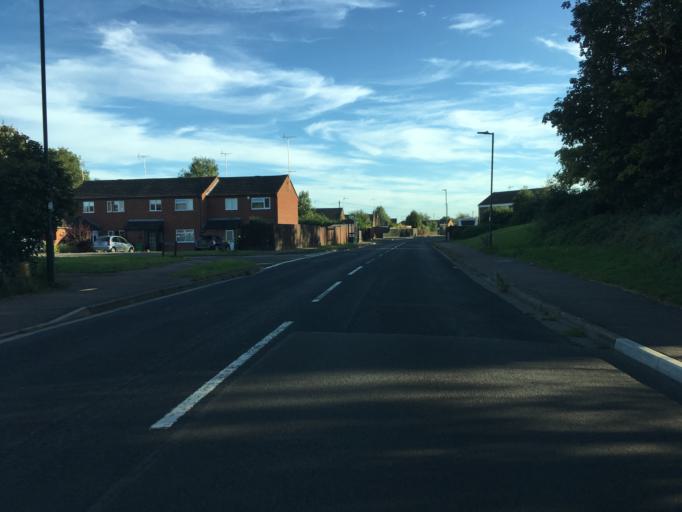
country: GB
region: England
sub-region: Worcestershire
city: Bredon
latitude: 52.0086
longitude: -2.1185
